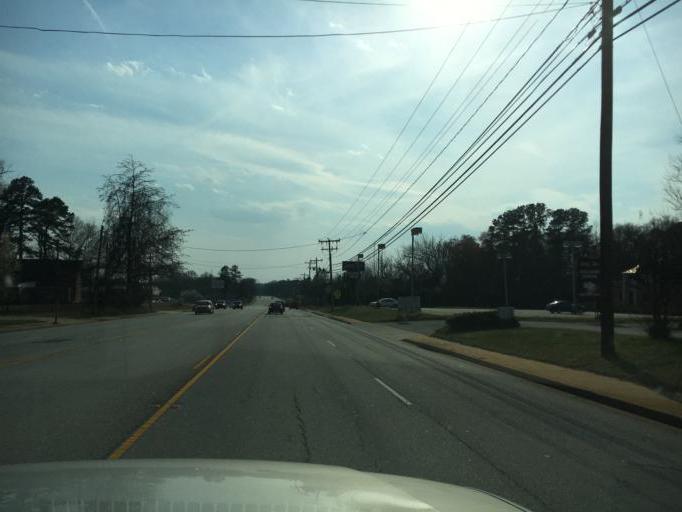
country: US
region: South Carolina
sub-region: Spartanburg County
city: Spartanburg
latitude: 34.9936
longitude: -81.9151
